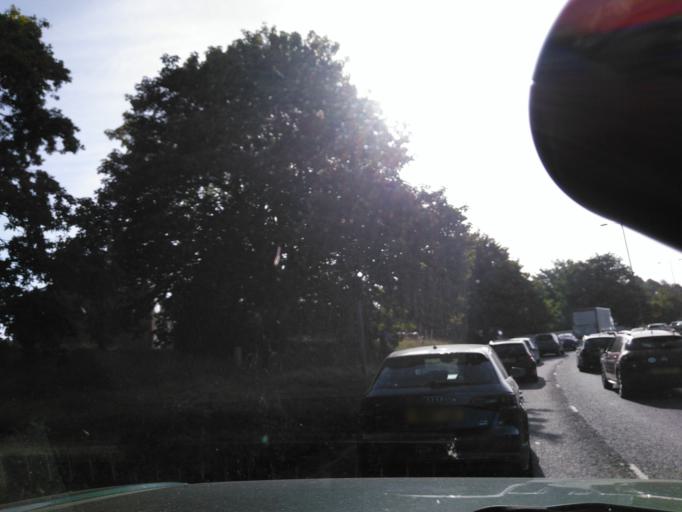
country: GB
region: England
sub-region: Wiltshire
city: Salisbury
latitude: 51.0769
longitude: -1.7942
